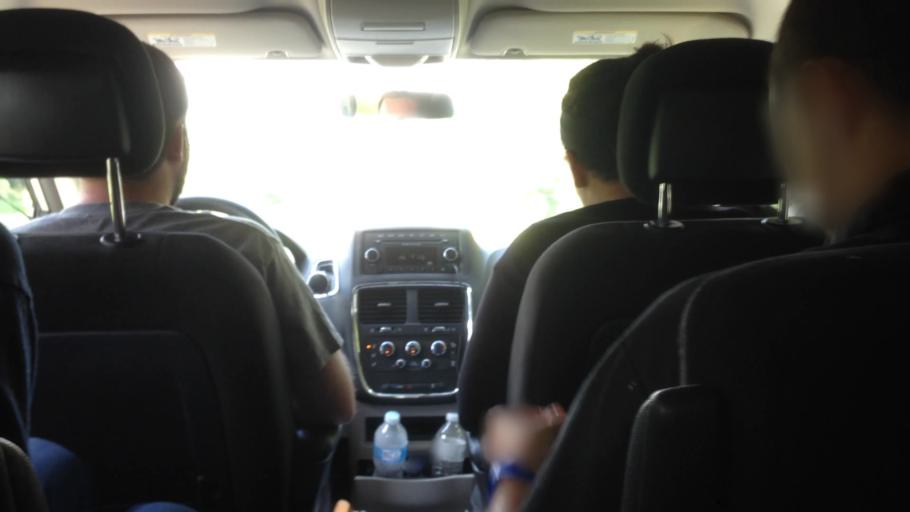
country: US
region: New York
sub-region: Dutchess County
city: Tivoli
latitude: 42.1182
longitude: -73.8911
